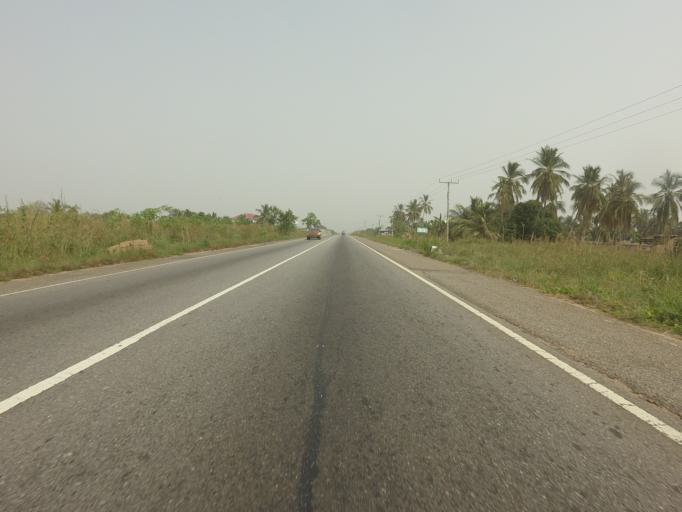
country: GH
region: Volta
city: Anloga
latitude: 5.8916
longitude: 0.4848
